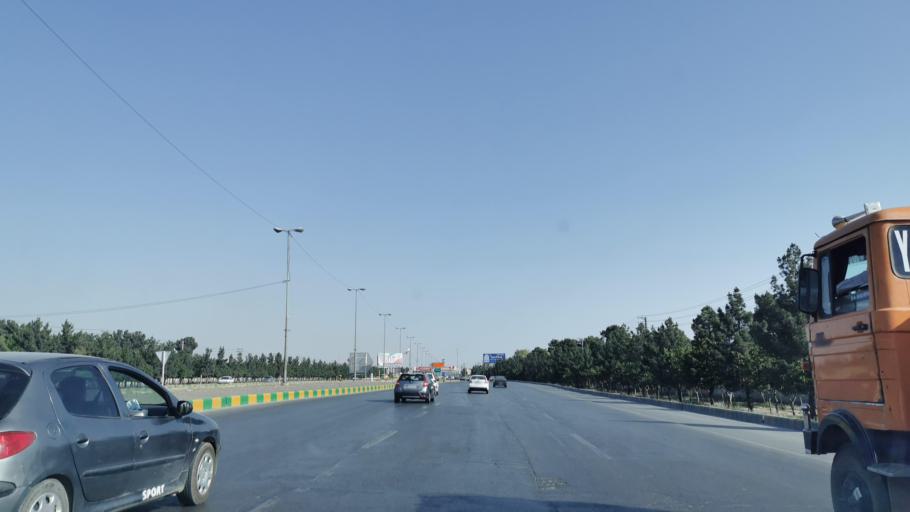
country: IR
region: Razavi Khorasan
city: Torqabeh
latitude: 36.4179
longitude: 59.4655
